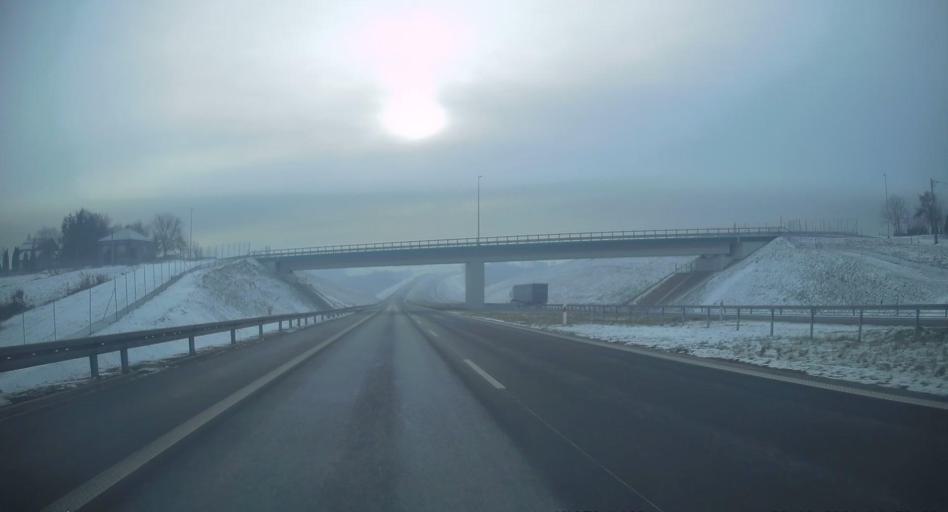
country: PL
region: Lesser Poland Voivodeship
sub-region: Powiat krakowski
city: Slomniki
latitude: 50.2655
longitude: 20.0204
